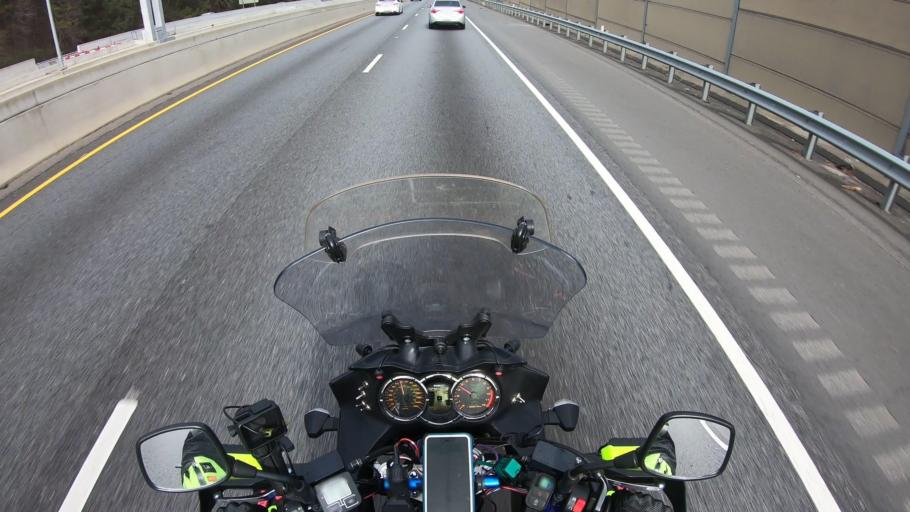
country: US
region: Georgia
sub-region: Cherokee County
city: Woodstock
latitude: 34.0610
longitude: -84.5384
